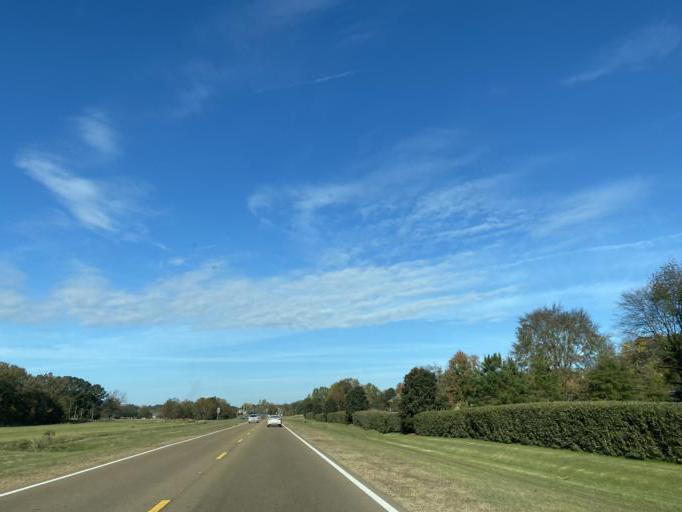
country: US
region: Mississippi
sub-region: Madison County
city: Madison
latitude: 32.4769
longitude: -90.1542
